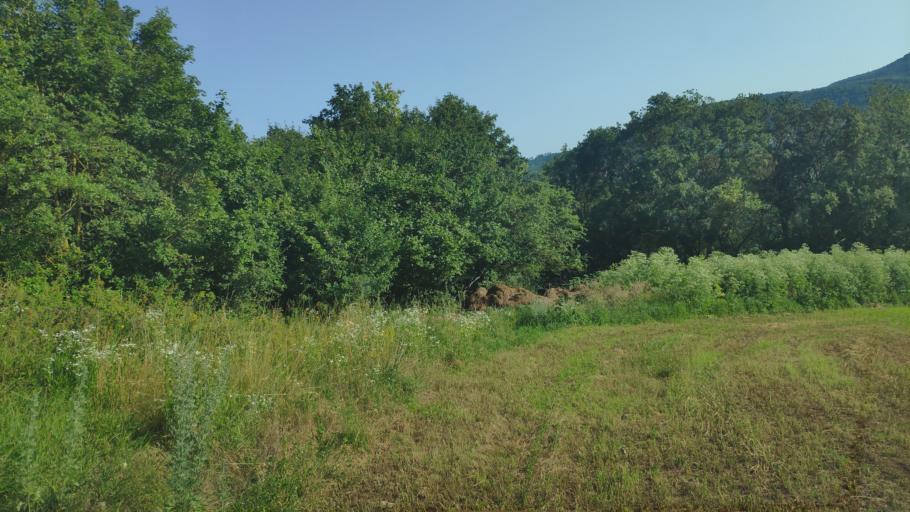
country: SK
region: Kosicky
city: Kosice
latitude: 48.8270
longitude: 21.2270
